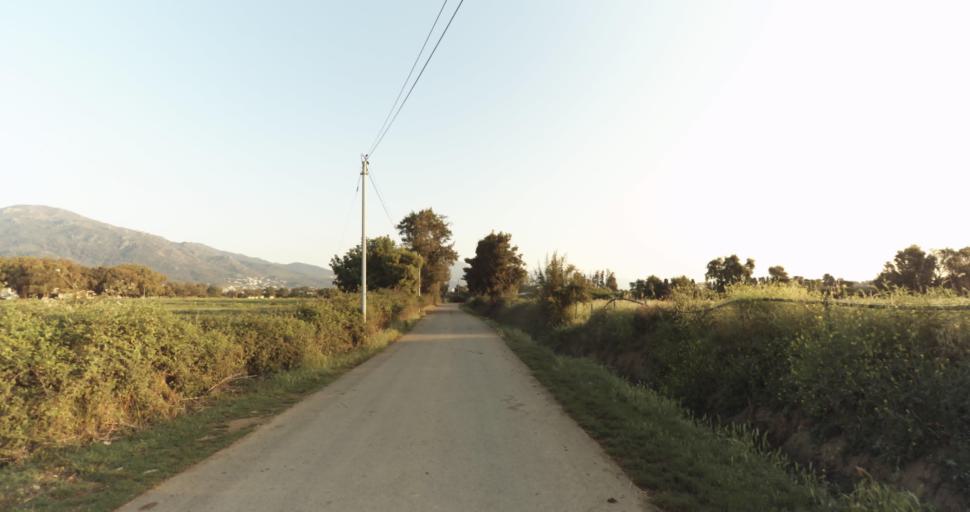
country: FR
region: Corsica
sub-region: Departement de la Haute-Corse
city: Biguglia
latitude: 42.6004
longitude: 9.4544
